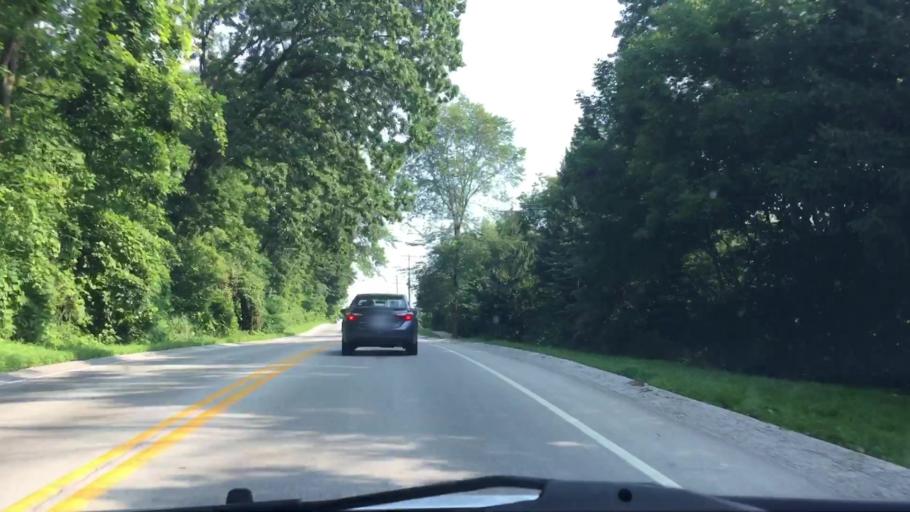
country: US
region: Wisconsin
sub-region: Waukesha County
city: Brookfield
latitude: 43.0488
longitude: -88.1463
